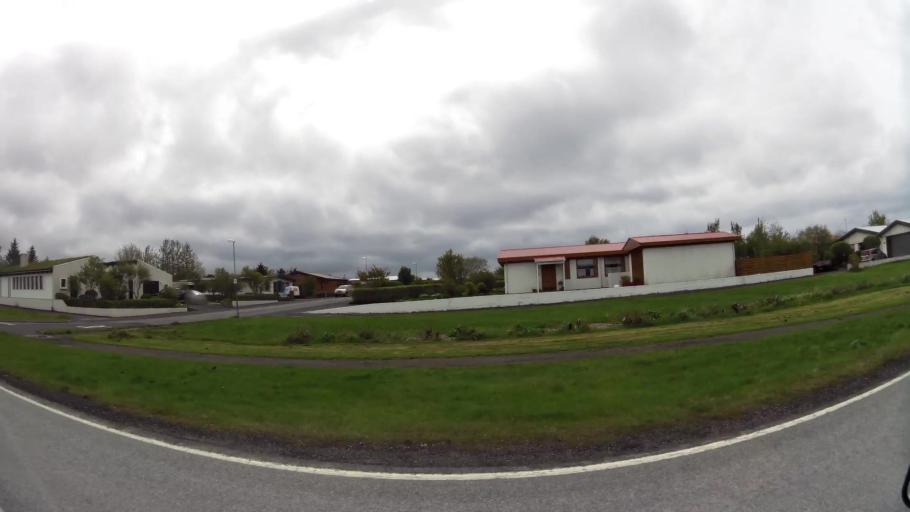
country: IS
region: Capital Region
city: Alftanes
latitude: 64.1100
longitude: -22.0145
